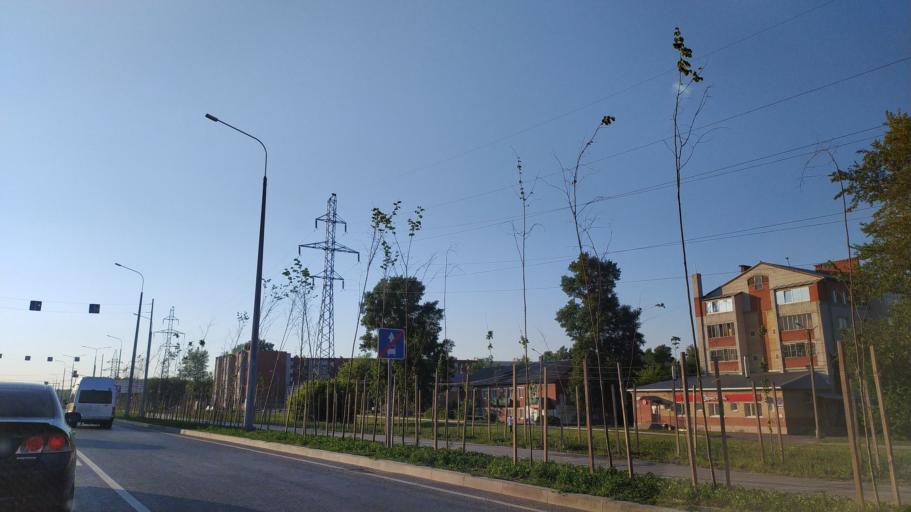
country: RU
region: Chuvashia
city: Kugesi
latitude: 56.0779
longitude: 47.2726
